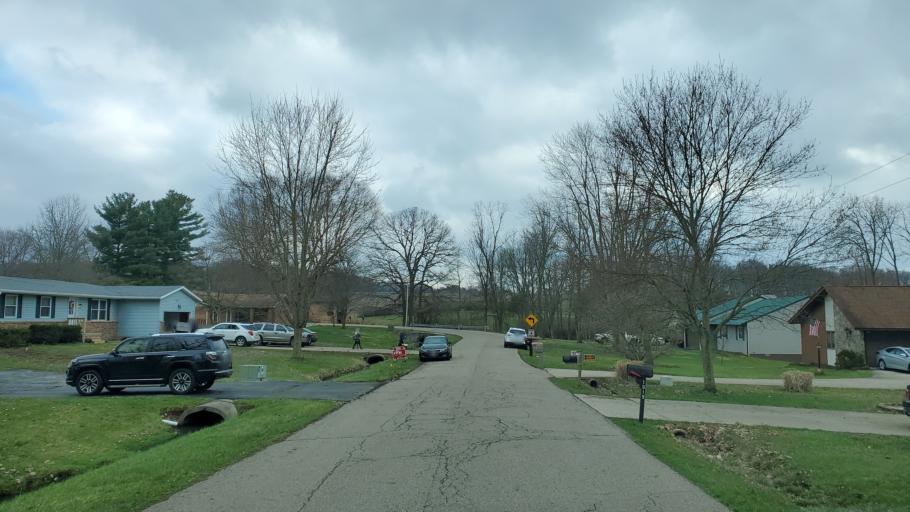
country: US
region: Ohio
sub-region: Licking County
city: Newark
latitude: 40.0224
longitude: -82.3831
